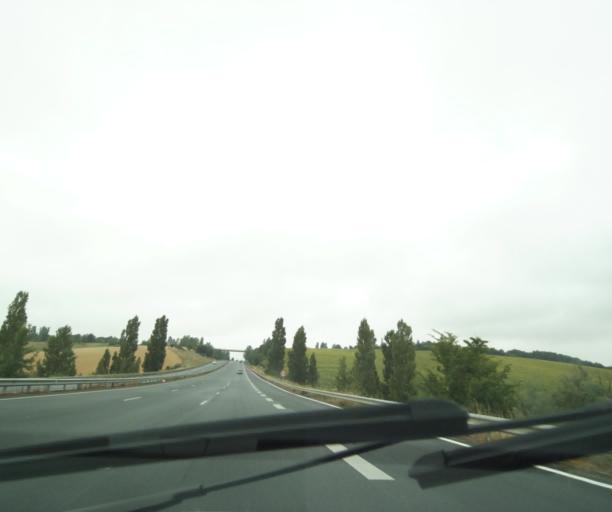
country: FR
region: Midi-Pyrenees
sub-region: Departement de la Haute-Garonne
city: Garidech
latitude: 43.7201
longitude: 1.5677
